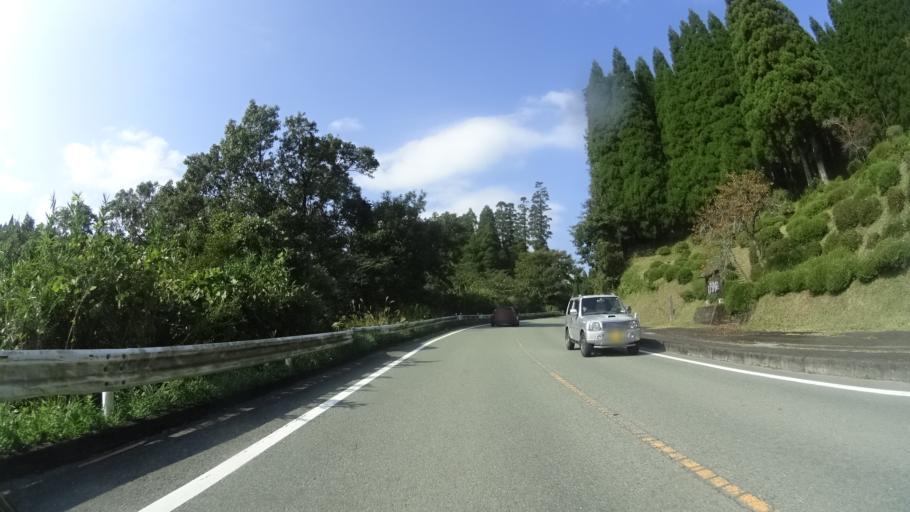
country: JP
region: Oita
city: Tsukawaki
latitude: 33.1362
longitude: 131.0890
